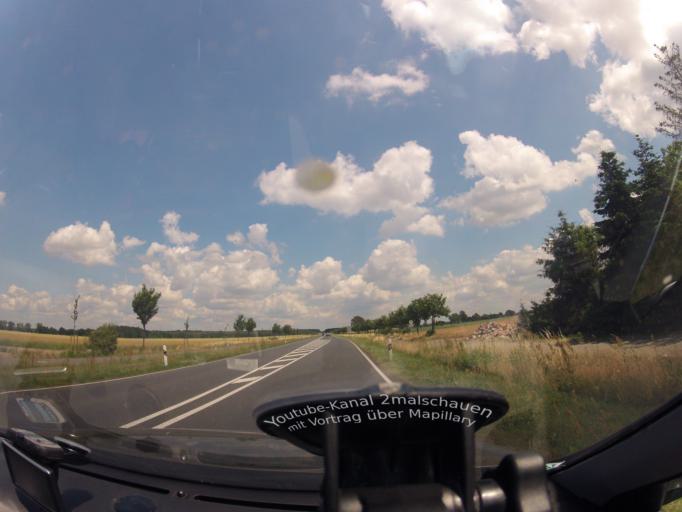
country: DE
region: Saxony
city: Mockrehna
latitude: 51.5117
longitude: 12.8283
